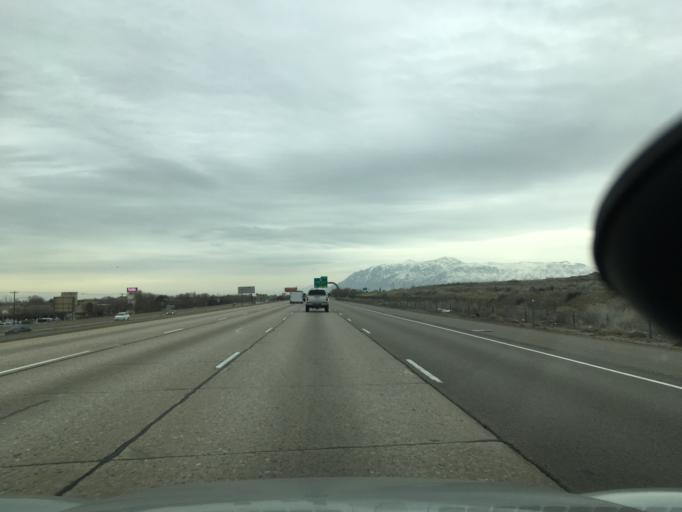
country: US
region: Utah
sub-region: Davis County
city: Sunset
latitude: 41.1482
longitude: -112.0251
